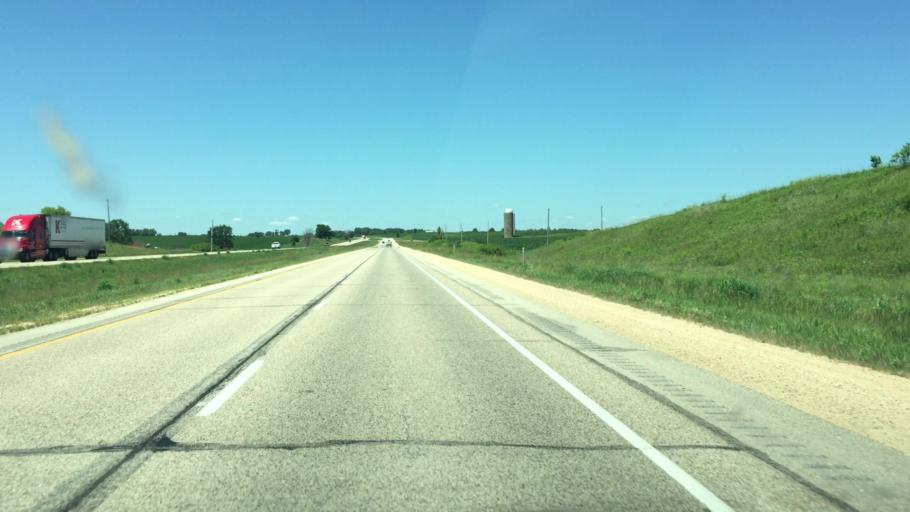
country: US
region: Iowa
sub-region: Jackson County
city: Maquoketa
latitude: 42.1990
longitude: -90.6690
